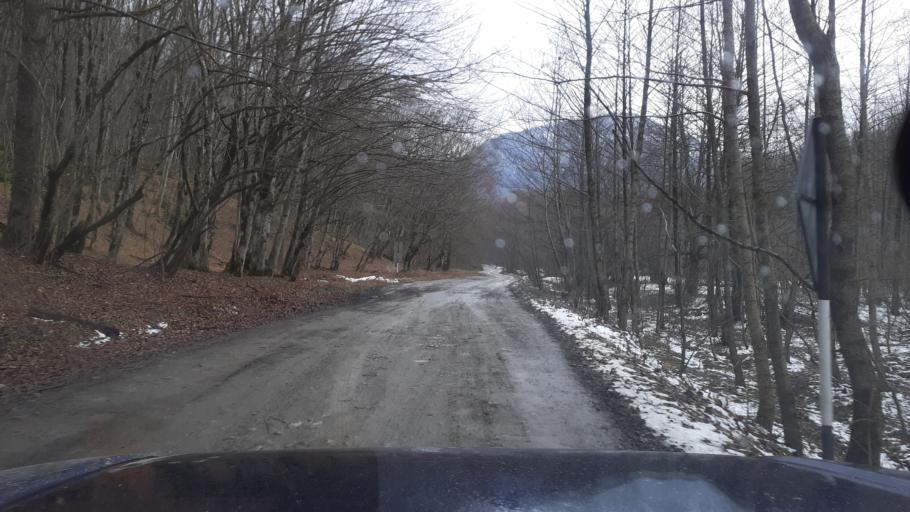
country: RU
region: Krasnodarskiy
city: Neftegorsk
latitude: 44.0708
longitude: 39.7110
